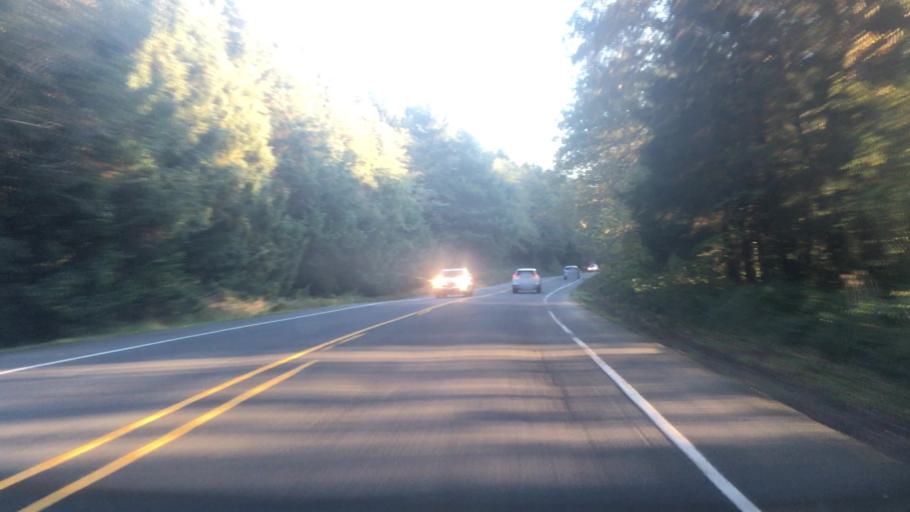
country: US
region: Oregon
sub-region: Clatsop County
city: Cannon Beach
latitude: 45.8794
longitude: -123.9577
